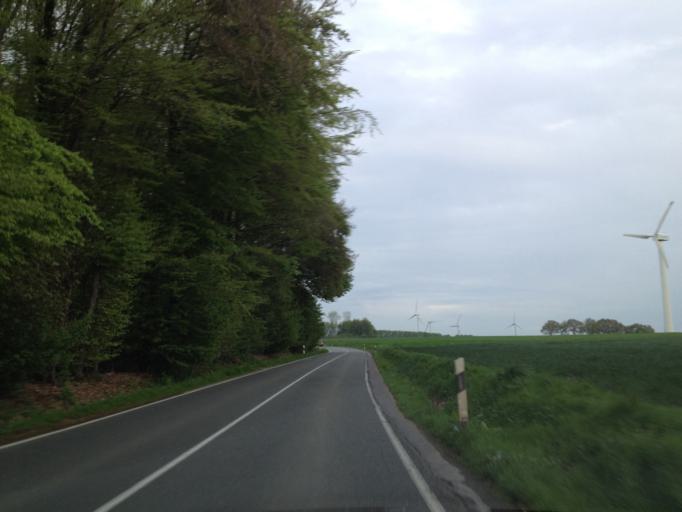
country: DE
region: North Rhine-Westphalia
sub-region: Regierungsbezirk Arnsberg
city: Mohnesee
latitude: 51.5097
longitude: 8.2204
